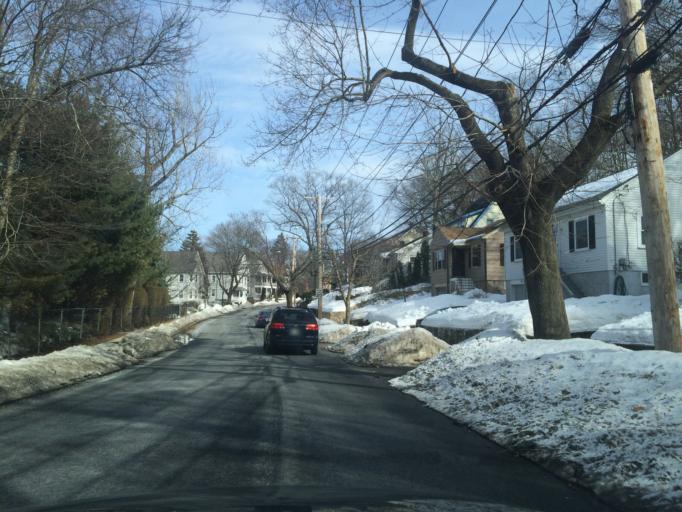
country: US
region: Massachusetts
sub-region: Middlesex County
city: Belmont
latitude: 42.4239
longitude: -71.1861
